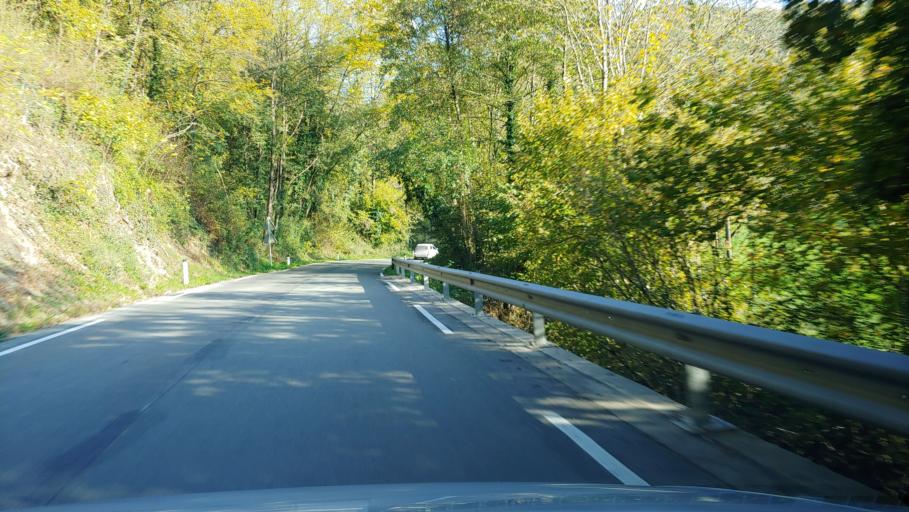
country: SI
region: Ajdovscina
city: Ajdovscina
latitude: 45.8136
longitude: 13.8932
